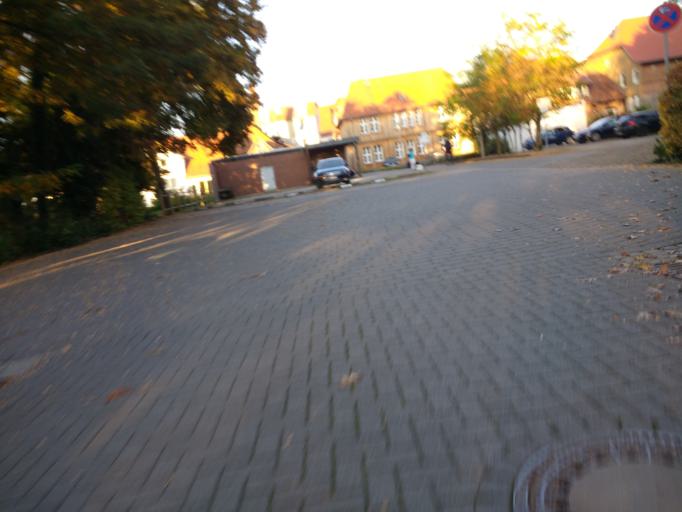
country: DE
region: Lower Saxony
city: Gifhorn
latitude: 52.4871
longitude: 10.5443
